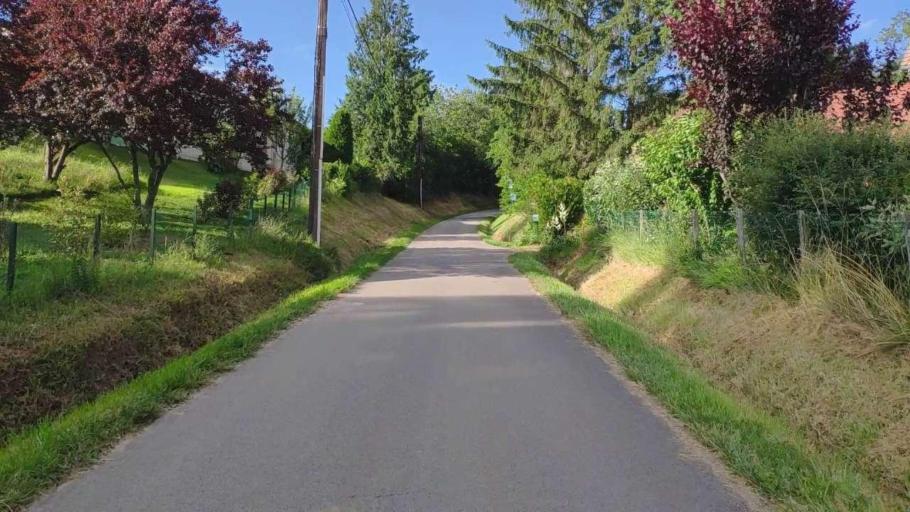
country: FR
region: Franche-Comte
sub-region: Departement du Jura
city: Bletterans
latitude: 46.7643
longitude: 5.5233
